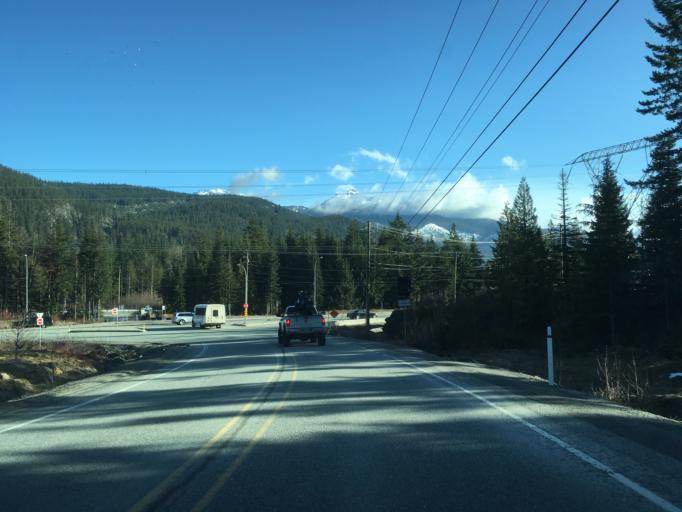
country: CA
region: British Columbia
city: Whistler
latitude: 50.0622
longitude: -123.1092
